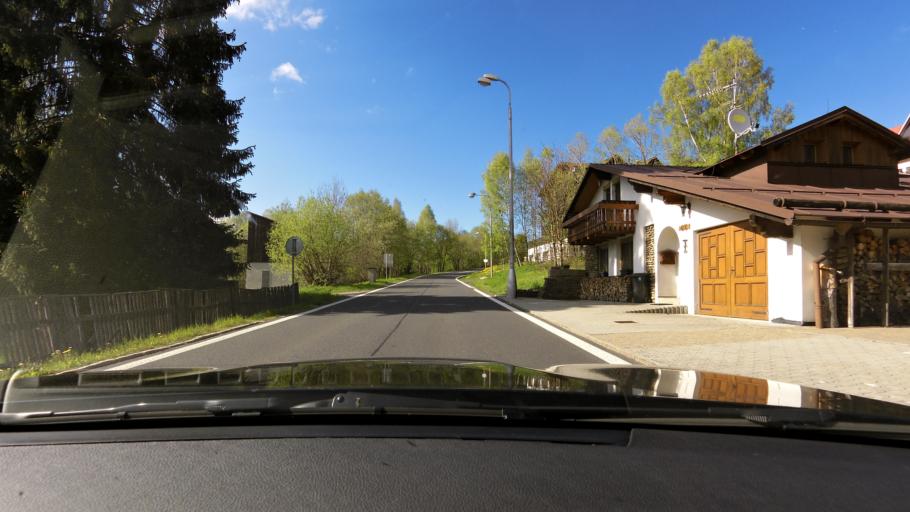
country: CZ
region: Plzensky
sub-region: Okres Klatovy
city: Zelezna Ruda
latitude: 49.1406
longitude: 13.2289
